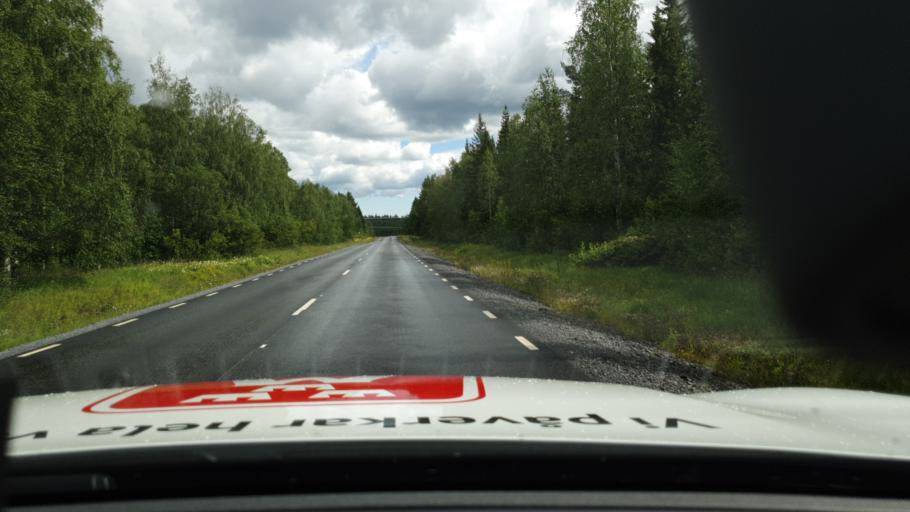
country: SE
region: Norrbotten
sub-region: Bodens Kommun
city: Saevast
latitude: 65.8445
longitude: 21.7770
